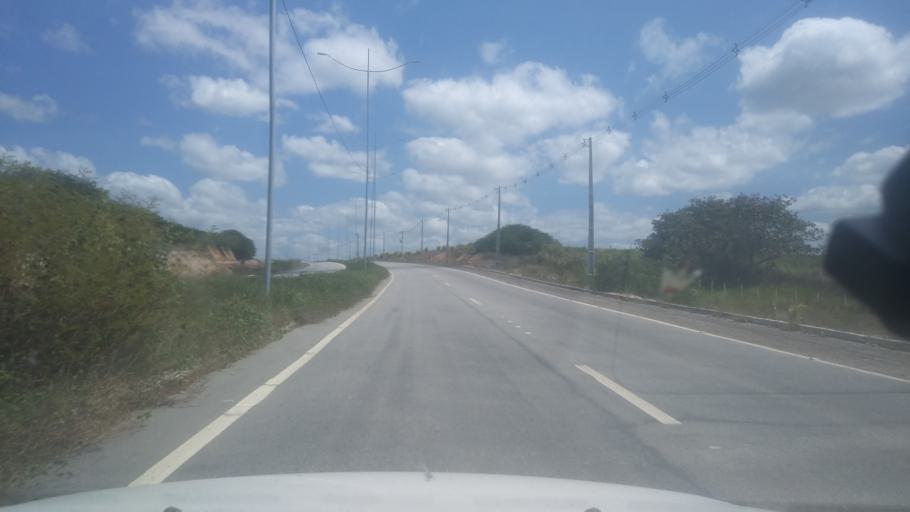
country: BR
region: Rio Grande do Norte
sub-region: Macaiba
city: Macaiba
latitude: -5.8355
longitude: -35.3736
